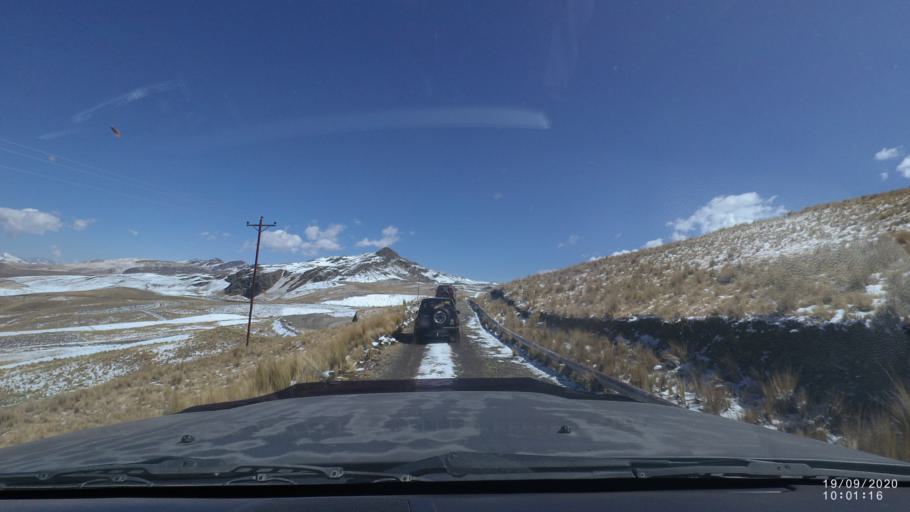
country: BO
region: Cochabamba
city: Cochabamba
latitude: -17.3022
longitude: -66.0910
